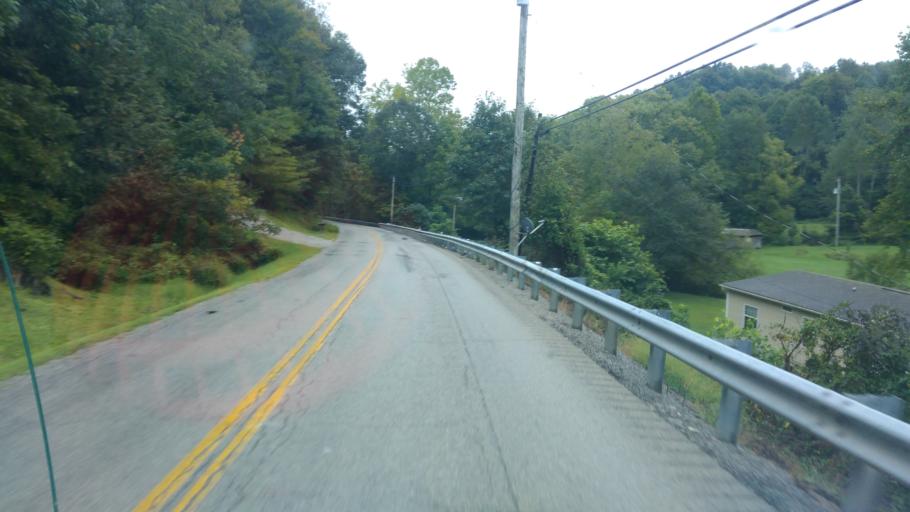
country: US
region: Kentucky
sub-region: Fleming County
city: Flemingsburg
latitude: 38.4502
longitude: -83.5173
